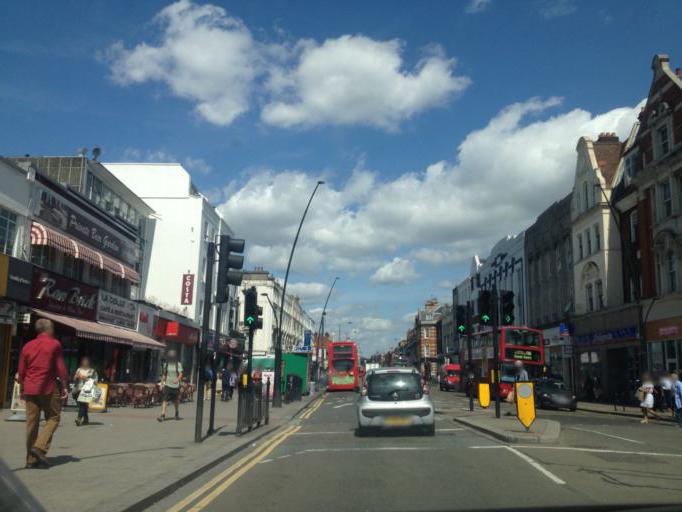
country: GB
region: England
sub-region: Greater London
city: Belsize Park
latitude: 51.5372
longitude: -0.1926
